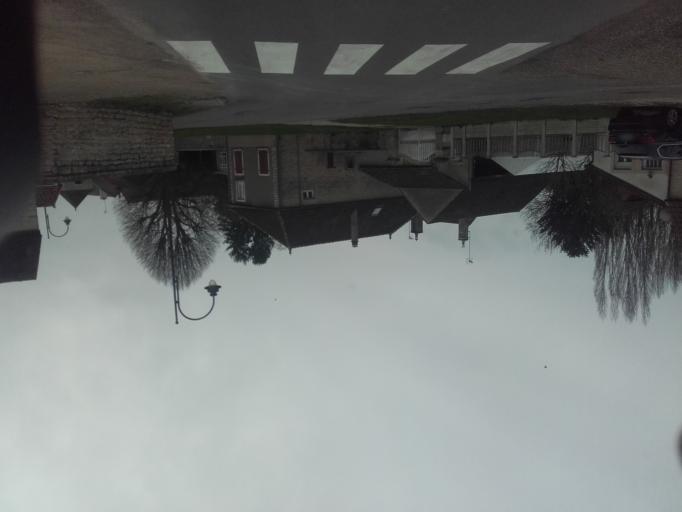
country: FR
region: Bourgogne
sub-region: Departement de Saone-et-Loire
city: Gergy
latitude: 46.9906
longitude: 4.9463
